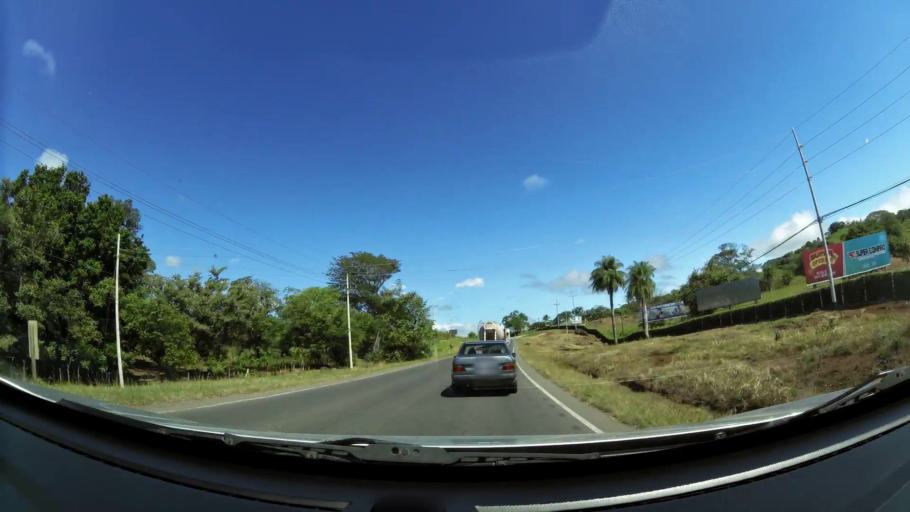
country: CR
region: Guanacaste
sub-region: Canton de Canas
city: Canas
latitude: 10.4066
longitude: -85.0862
